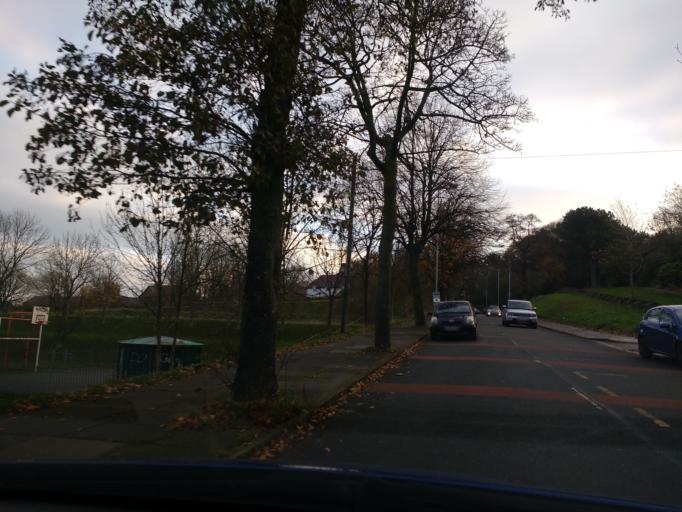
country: GB
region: England
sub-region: Lancashire
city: Lancaster
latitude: 54.0475
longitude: -2.7842
